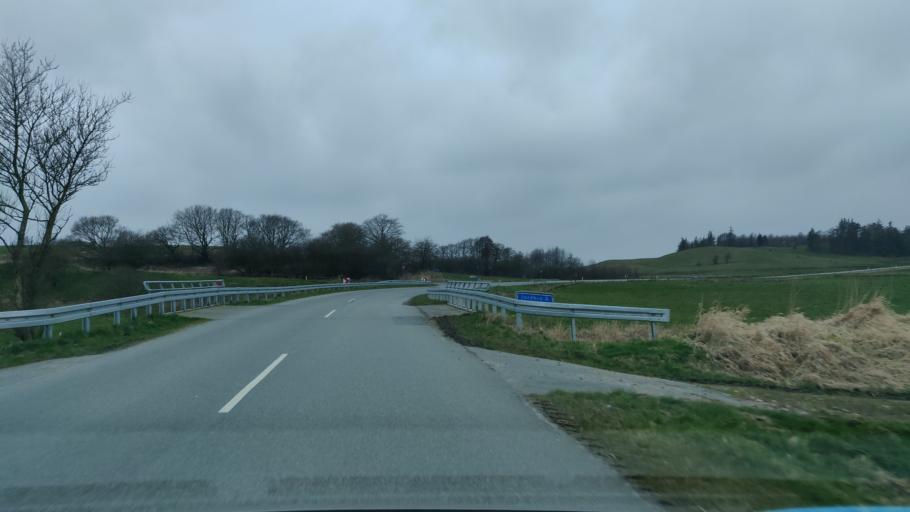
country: DK
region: Central Jutland
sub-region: Skive Kommune
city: Hojslev
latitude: 56.5703
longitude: 9.2400
